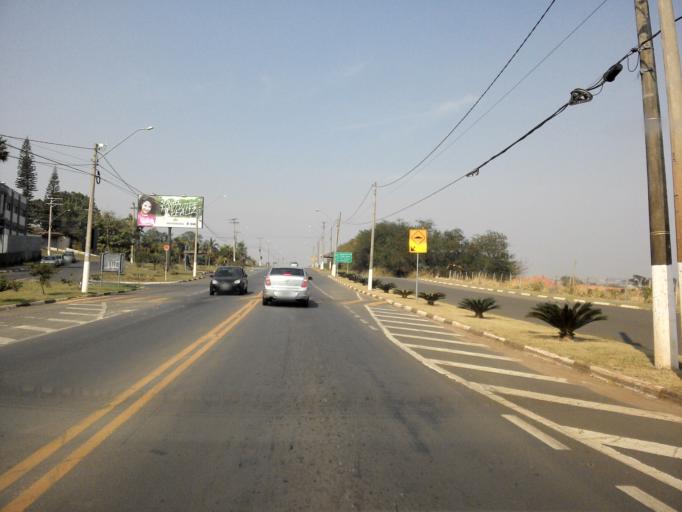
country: BR
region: Sao Paulo
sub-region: Hortolandia
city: Hortolandia
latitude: -22.8467
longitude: -47.2400
